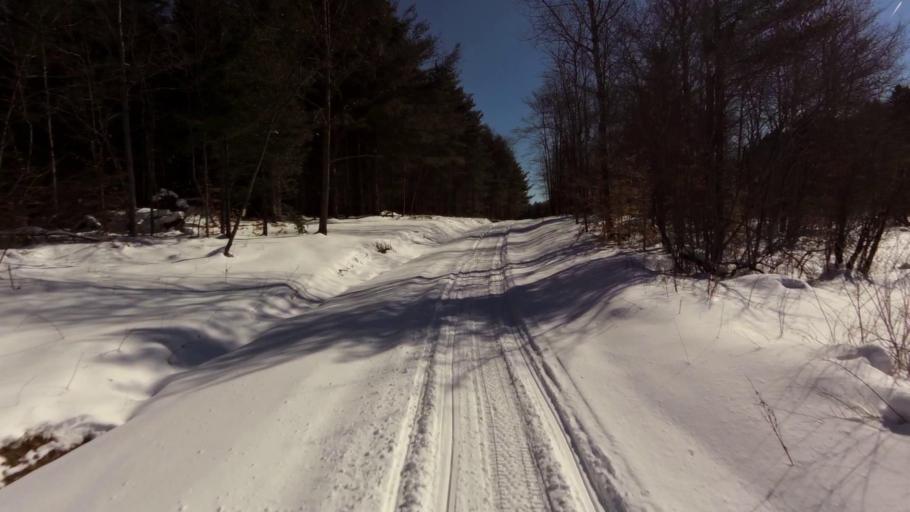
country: US
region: New York
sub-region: Allegany County
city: Cuba
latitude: 42.3051
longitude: -78.2525
